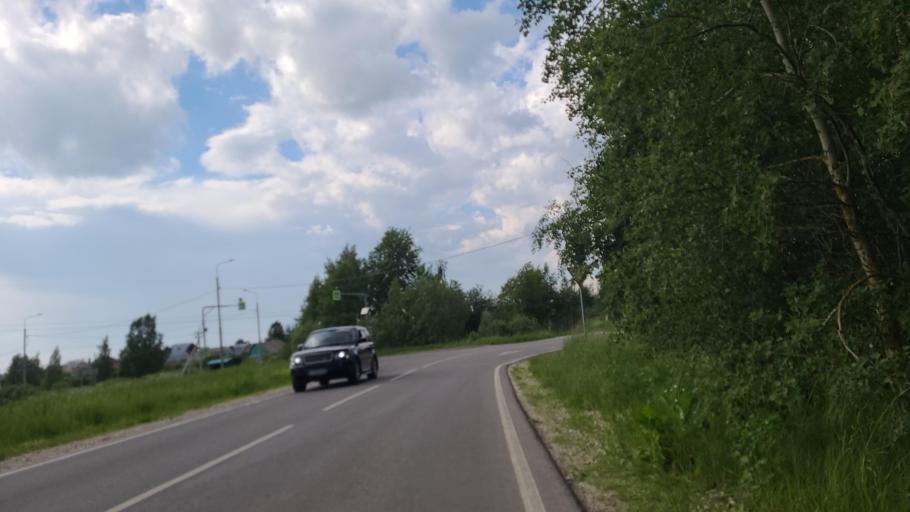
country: RU
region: Moskovskaya
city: Konobeyevo
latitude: 55.4016
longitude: 38.6756
